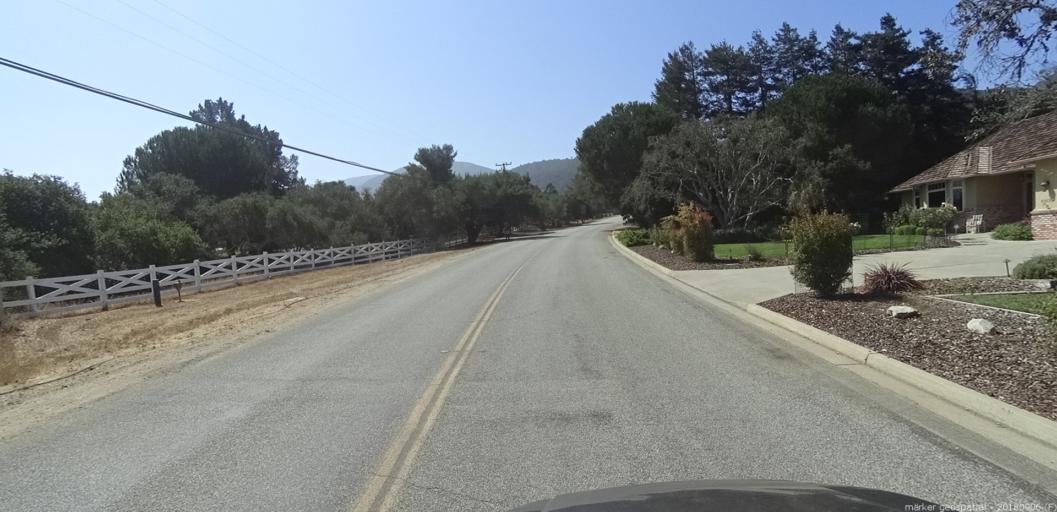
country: US
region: California
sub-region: Monterey County
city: Salinas
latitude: 36.5854
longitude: -121.6299
